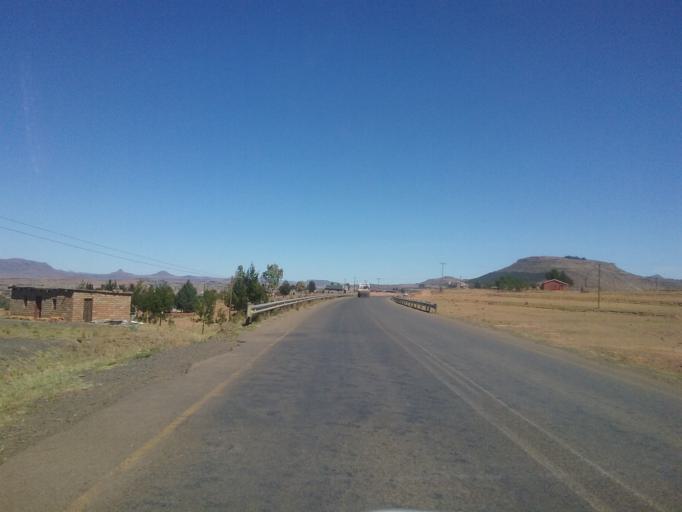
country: LS
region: Quthing
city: Quthing
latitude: -30.3927
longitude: 27.6307
